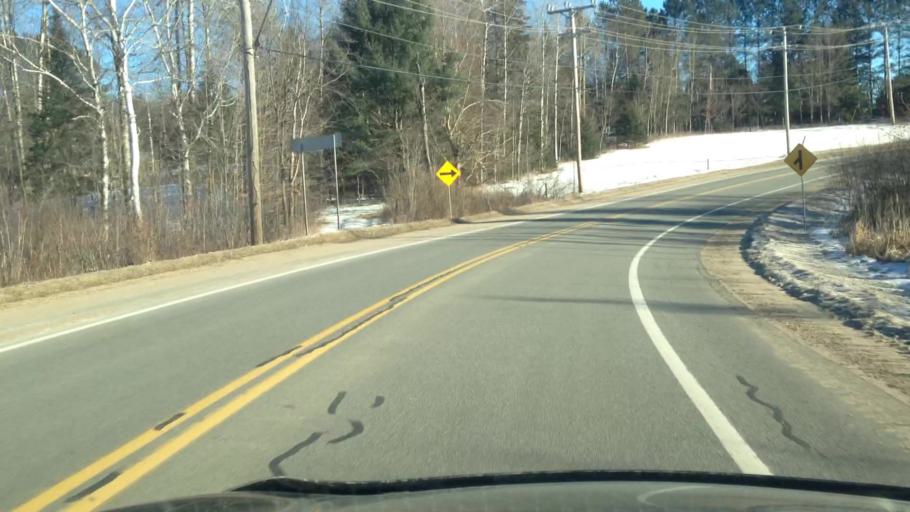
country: CA
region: Quebec
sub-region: Laurentides
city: Mont-Tremblant
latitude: 45.9889
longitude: -74.6121
